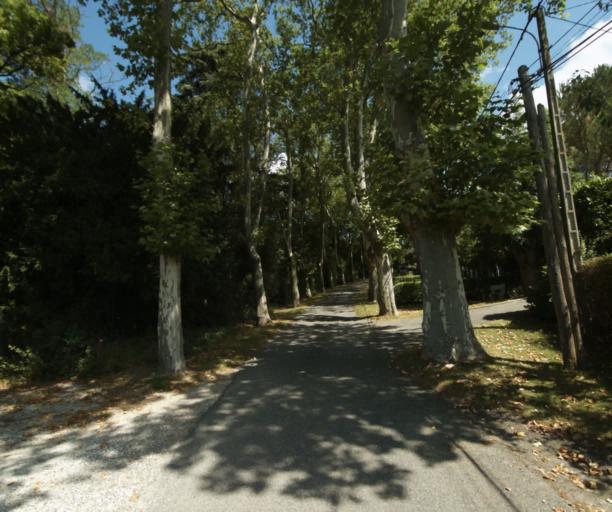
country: FR
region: Midi-Pyrenees
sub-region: Departement de la Haute-Garonne
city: Auriac-sur-Vendinelle
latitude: 43.4645
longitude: 1.7939
